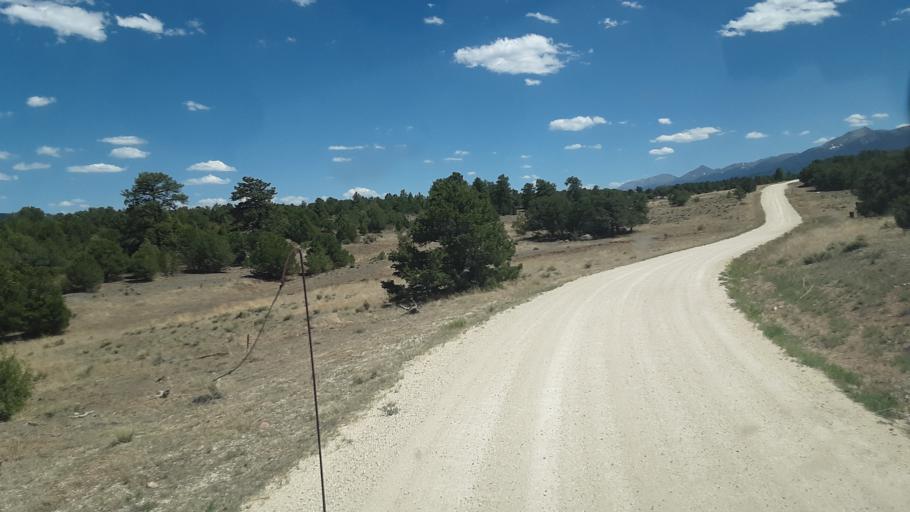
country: US
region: Colorado
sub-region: Custer County
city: Westcliffe
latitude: 38.3216
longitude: -105.6249
